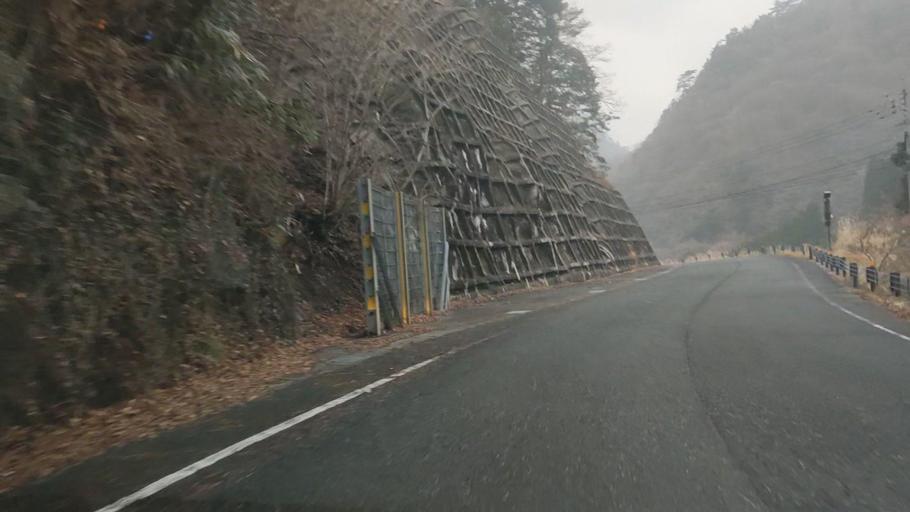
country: JP
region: Kumamoto
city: Matsubase
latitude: 32.5484
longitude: 130.9390
